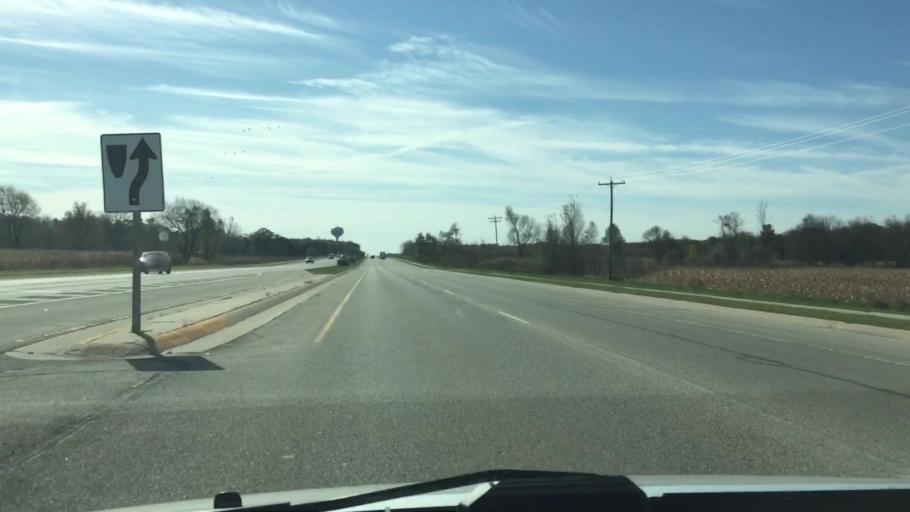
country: US
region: Wisconsin
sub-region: Waukesha County
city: Sussex
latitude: 43.1300
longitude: -88.2442
